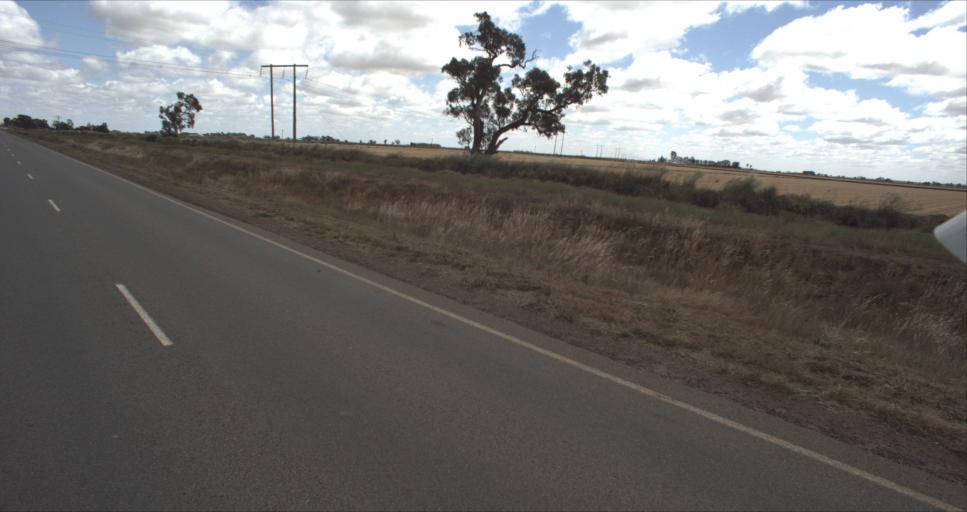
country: AU
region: New South Wales
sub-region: Murrumbidgee Shire
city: Darlington Point
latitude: -34.4966
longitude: 146.1841
